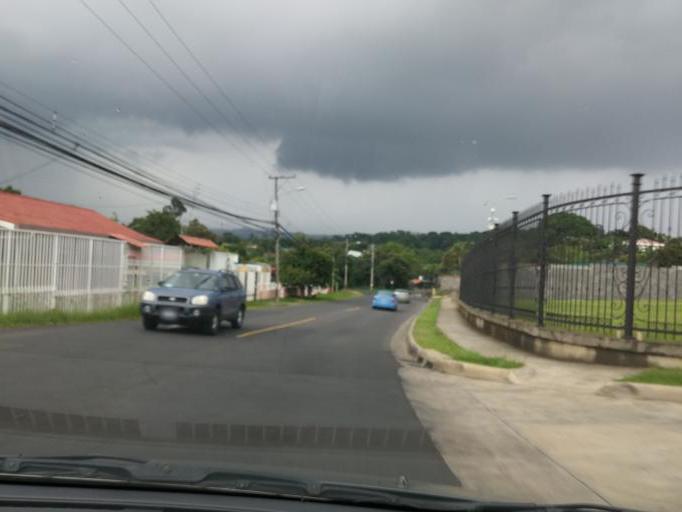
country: CR
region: Heredia
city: Llorente
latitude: 10.0166
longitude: -84.1544
